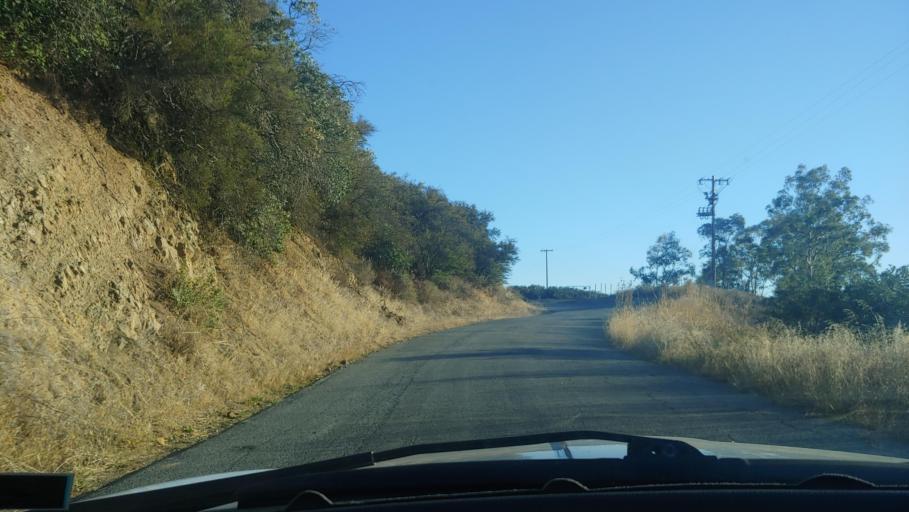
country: US
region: California
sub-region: Santa Barbara County
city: Goleta
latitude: 34.5154
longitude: -119.7947
